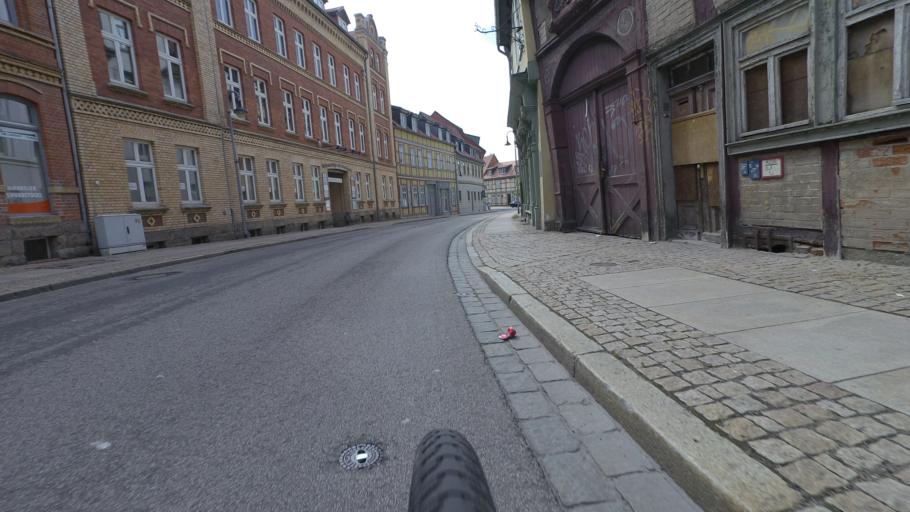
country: DE
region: Saxony-Anhalt
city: Halberstadt
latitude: 51.8945
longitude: 11.0439
